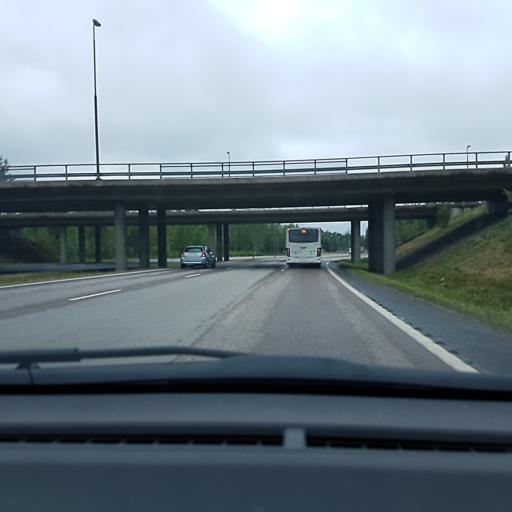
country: FI
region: Uusimaa
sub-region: Helsinki
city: Kerava
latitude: 60.3442
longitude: 25.1115
